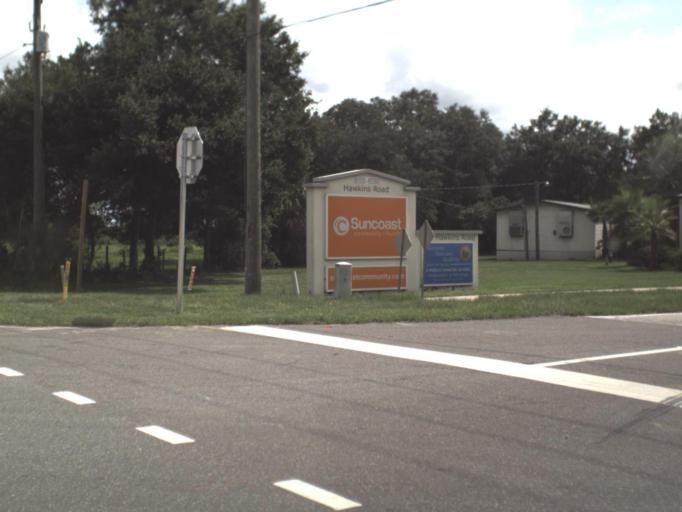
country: US
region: Florida
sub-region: Sarasota County
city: Lake Sarasota
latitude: 27.2629
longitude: -82.4095
